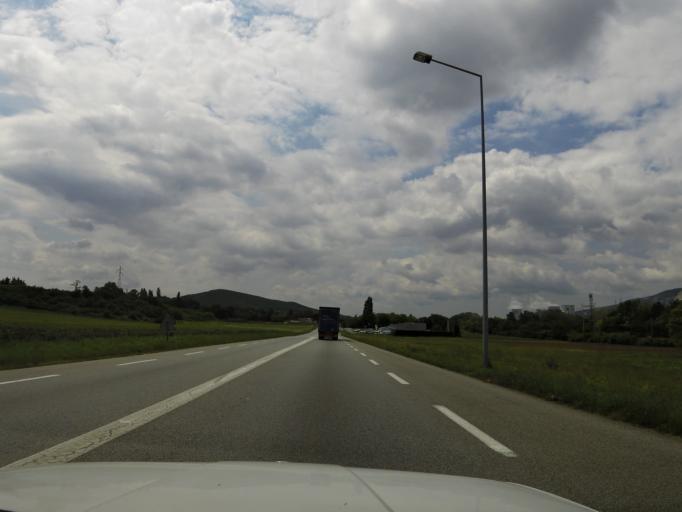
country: FR
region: Rhone-Alpes
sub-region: Departement de l'Ardeche
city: Cruas
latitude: 44.6598
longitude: 4.7888
